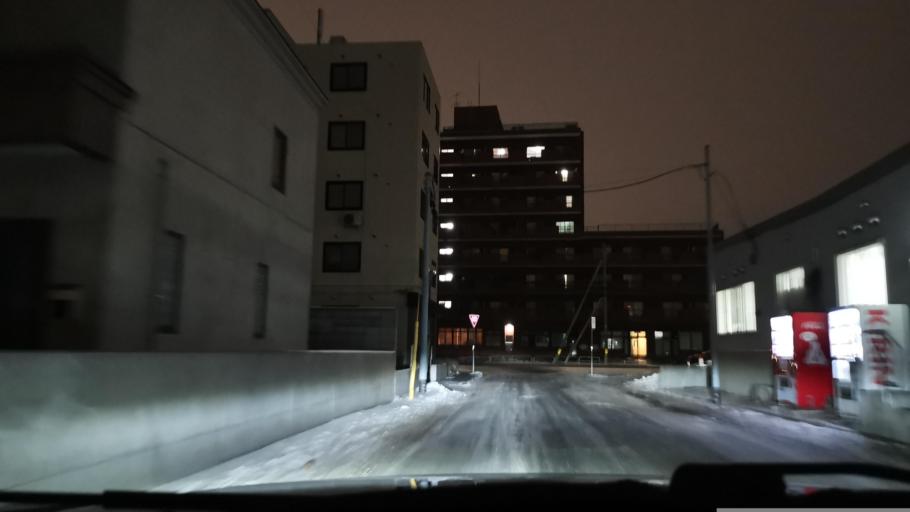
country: JP
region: Hokkaido
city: Sapporo
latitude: 43.0663
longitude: 141.3985
